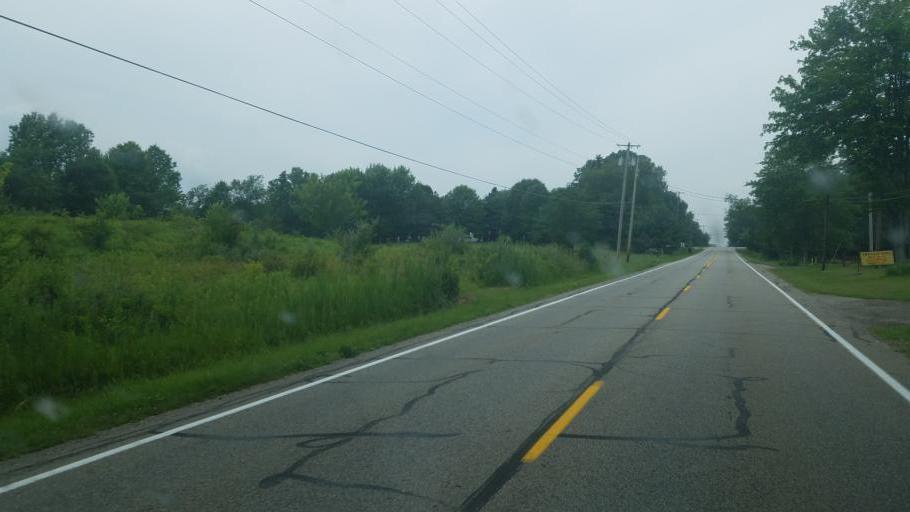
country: US
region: Ohio
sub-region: Portage County
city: Brimfield
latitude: 41.0997
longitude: -81.3141
